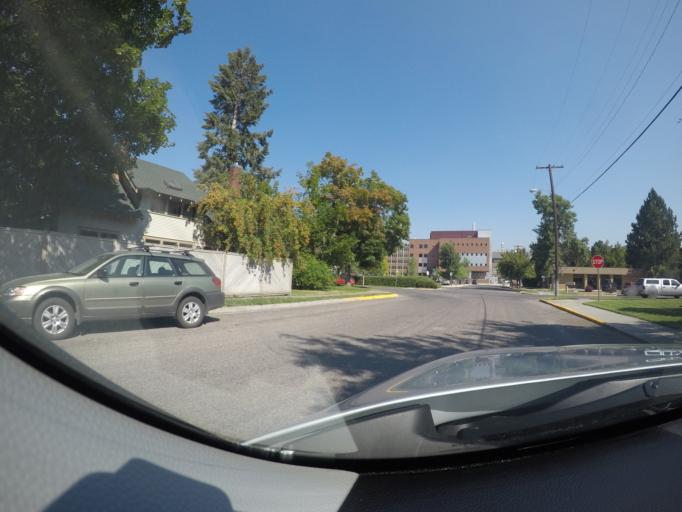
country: US
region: Montana
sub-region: Missoula County
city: Missoula
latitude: 46.8568
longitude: -113.9854
